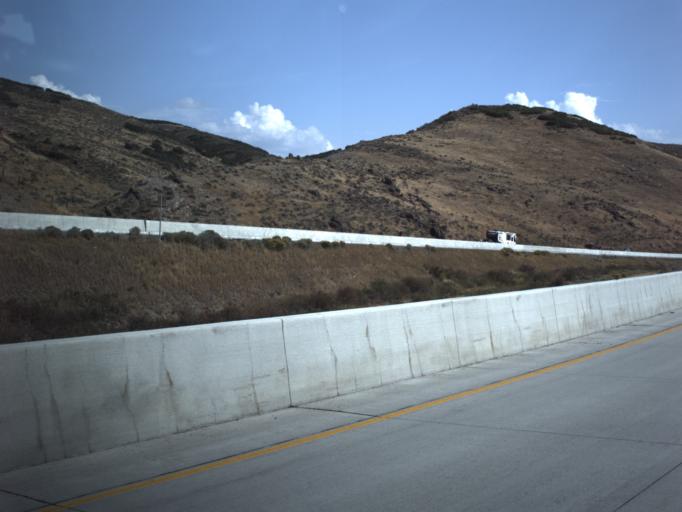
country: US
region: Utah
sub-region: Summit County
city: Snyderville
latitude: 40.7564
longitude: -111.4722
